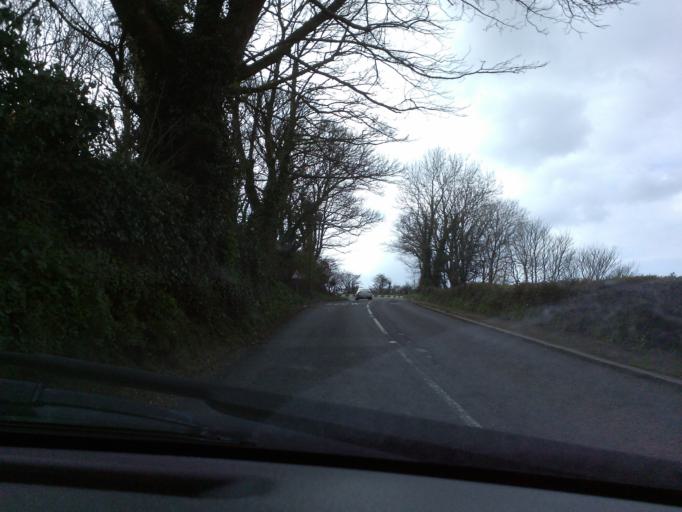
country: GB
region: England
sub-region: Cornwall
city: Penzance
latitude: 50.1066
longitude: -5.5742
